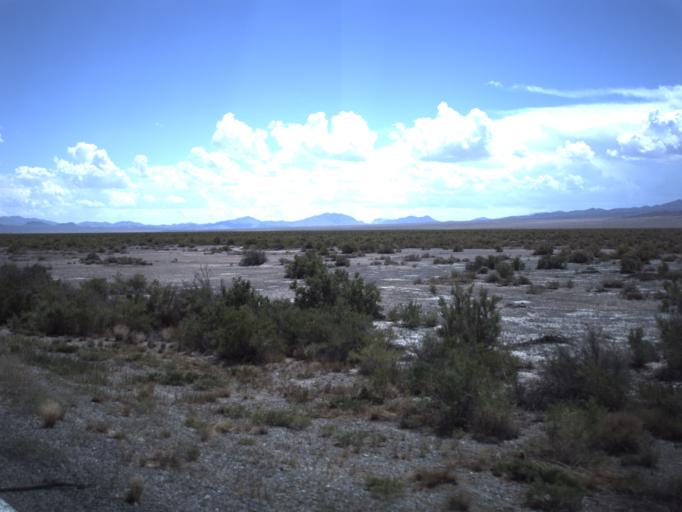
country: US
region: Nevada
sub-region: White Pine County
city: McGill
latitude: 39.0477
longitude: -113.9261
